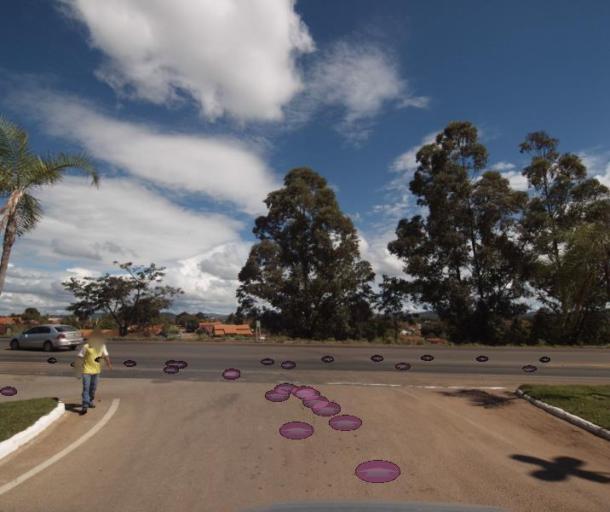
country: BR
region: Goias
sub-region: Uruacu
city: Uruacu
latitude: -14.5219
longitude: -49.1569
